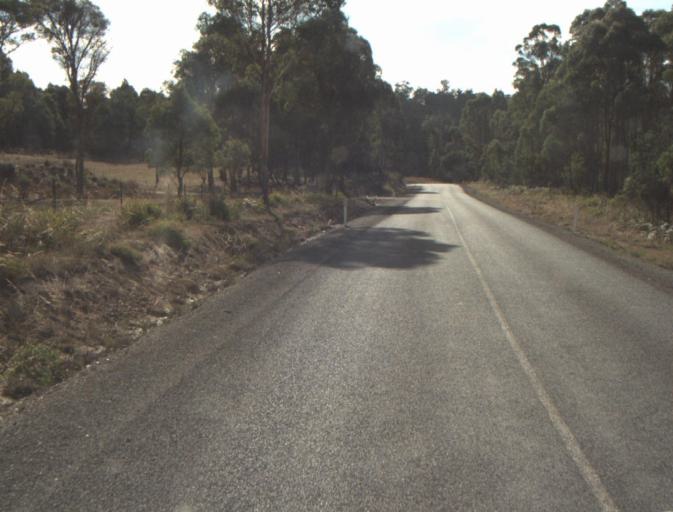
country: AU
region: Tasmania
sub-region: Launceston
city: Mayfield
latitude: -41.2100
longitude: 147.1314
